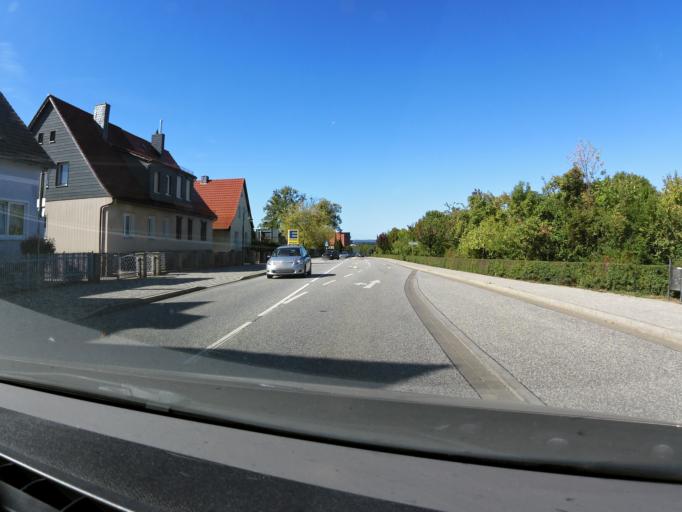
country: DE
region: Saxony-Anhalt
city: Gernrode
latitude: 51.7270
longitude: 11.1443
